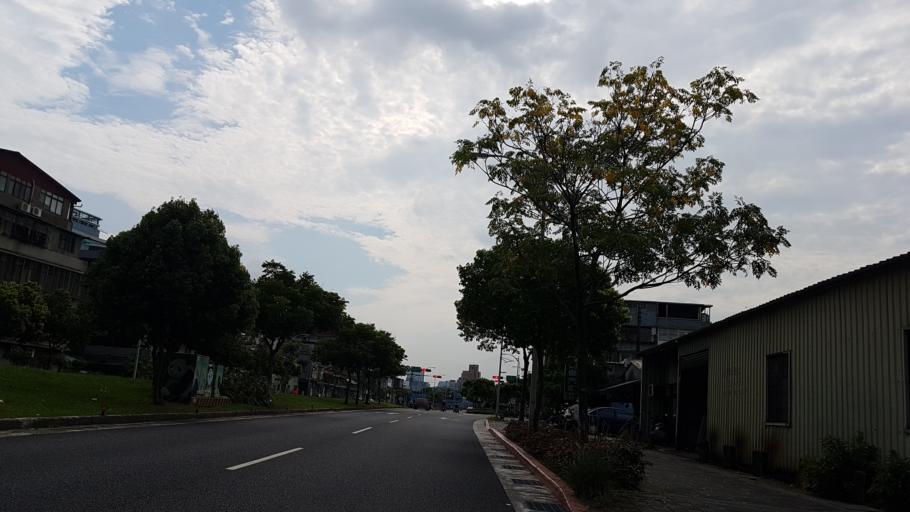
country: TW
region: Taipei
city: Taipei
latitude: 25.0541
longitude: 121.6140
